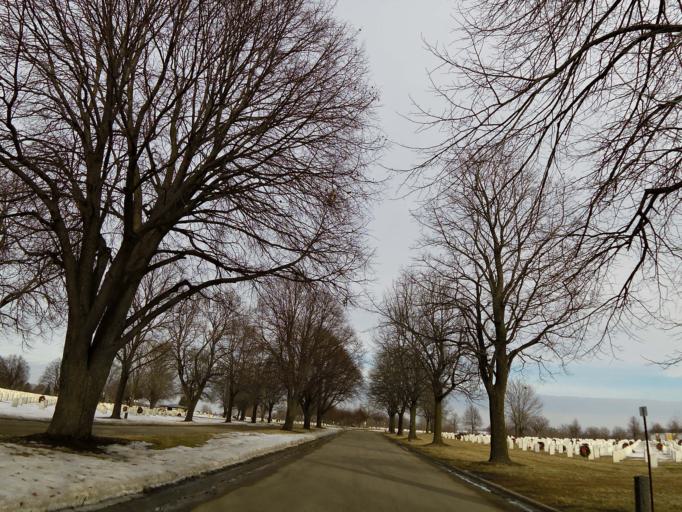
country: US
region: Minnesota
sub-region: Hennepin County
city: Richfield
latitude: 44.8664
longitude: -93.2180
